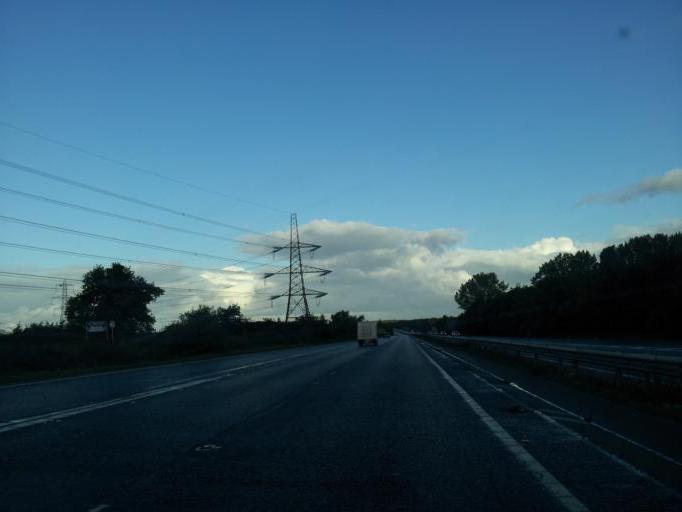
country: GB
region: England
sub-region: Norfolk
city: Cringleford
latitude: 52.6062
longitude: 1.2212
